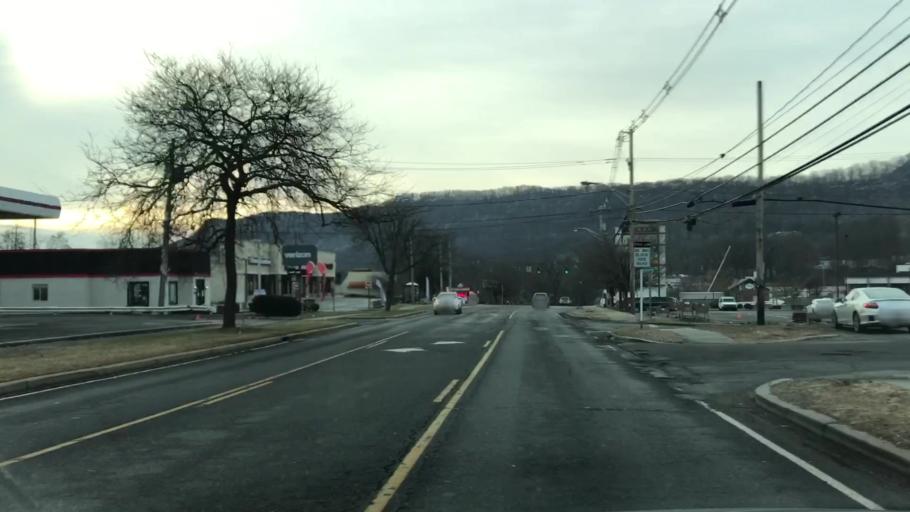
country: US
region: New York
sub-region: Rockland County
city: West Haverstraw
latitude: 41.2075
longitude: -73.9849
